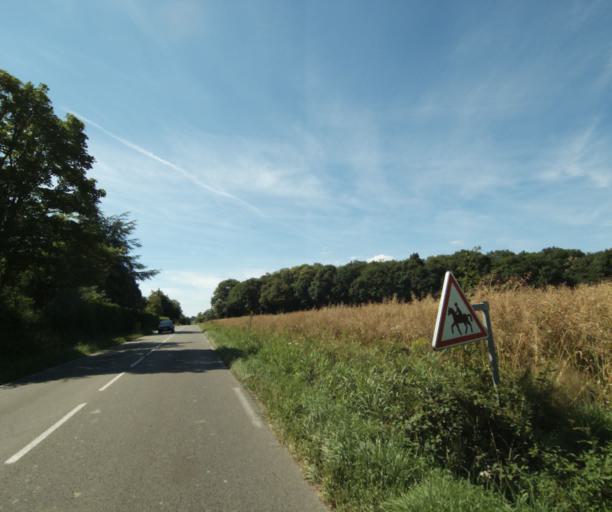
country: FR
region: Pays de la Loire
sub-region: Departement de la Mayenne
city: Laval
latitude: 48.0451
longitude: -0.7803
